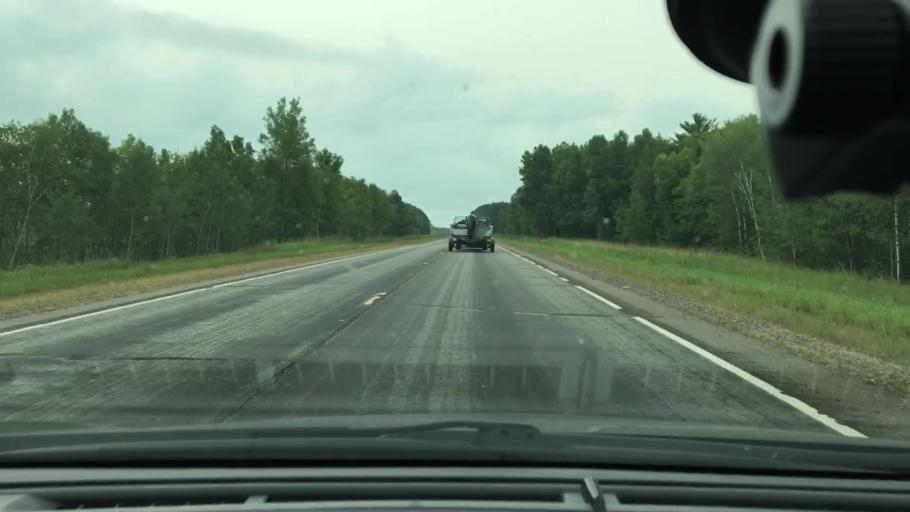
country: US
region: Minnesota
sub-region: Crow Wing County
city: Crosby
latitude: 46.6412
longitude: -93.9508
